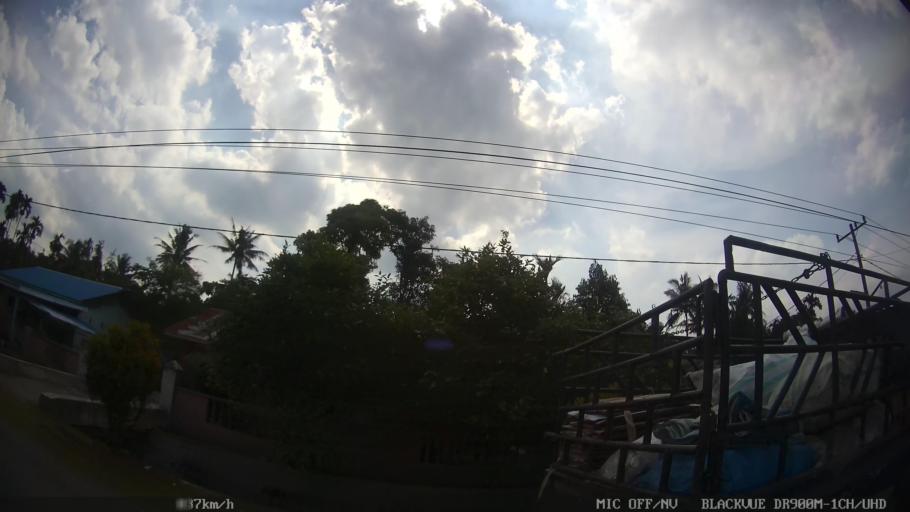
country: ID
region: North Sumatra
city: Binjai
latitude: 3.6392
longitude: 98.5176
